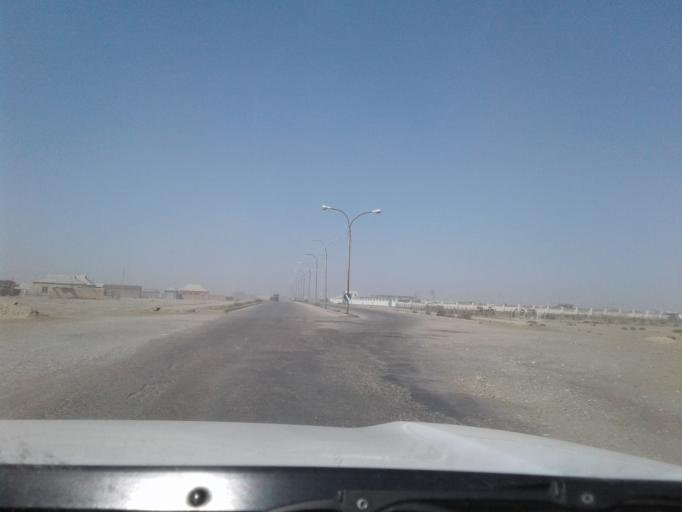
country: TM
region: Balkan
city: Gumdag
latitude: 39.1860
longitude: 54.5844
